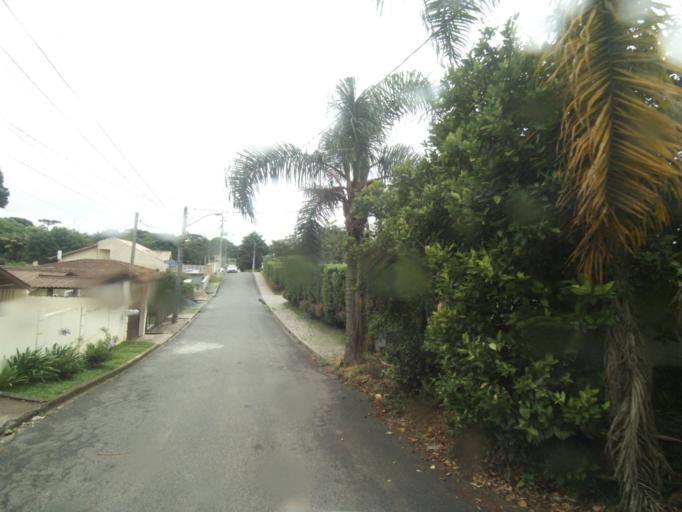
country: BR
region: Parana
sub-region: Curitiba
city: Curitiba
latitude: -25.4254
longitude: -49.3155
